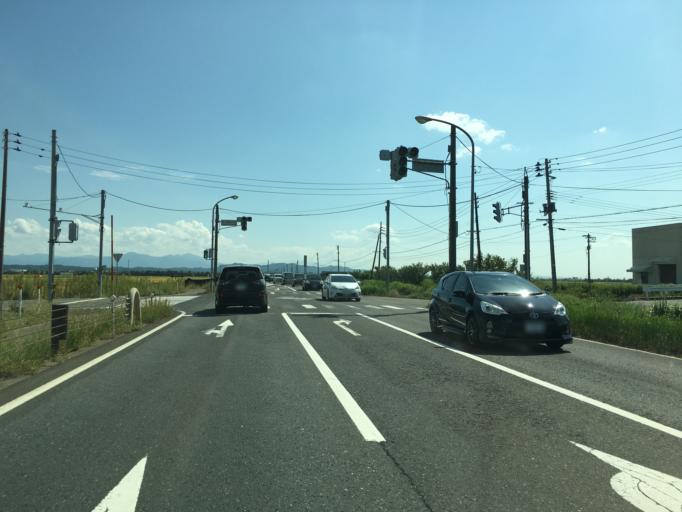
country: JP
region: Niigata
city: Niitsu-honcho
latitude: 37.8324
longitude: 139.0969
